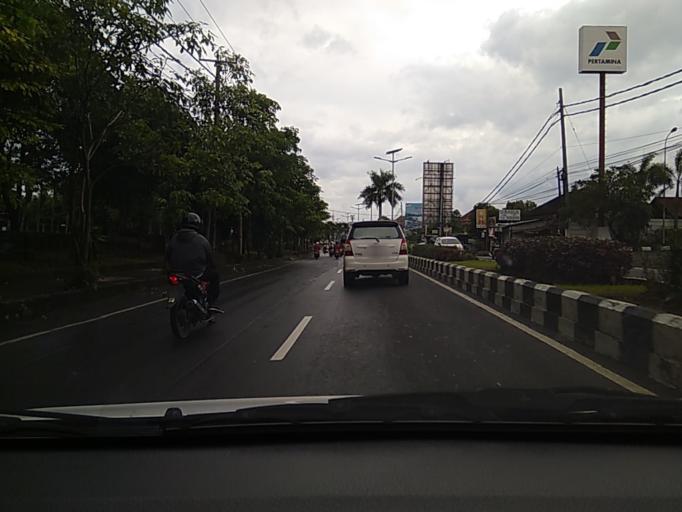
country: ID
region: Bali
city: Bualu
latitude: -8.7849
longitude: 115.1970
